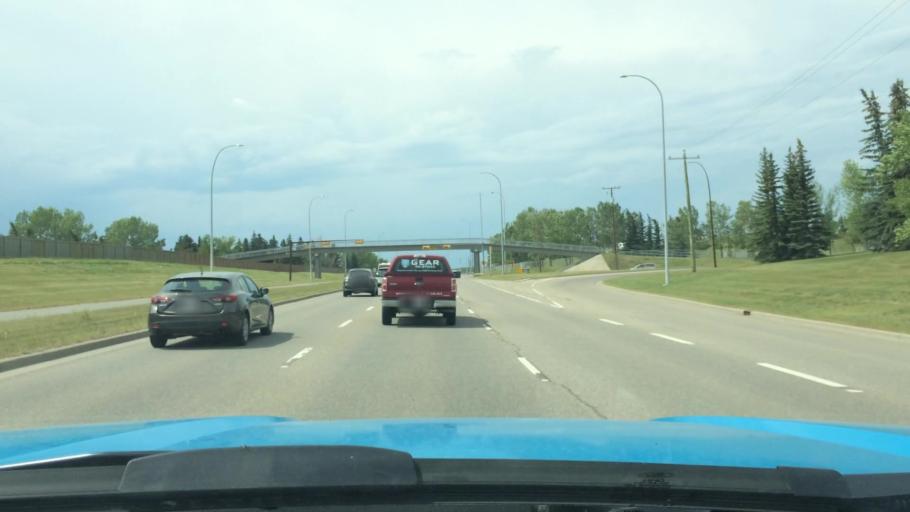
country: CA
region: Alberta
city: Calgary
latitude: 51.1118
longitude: -114.1463
